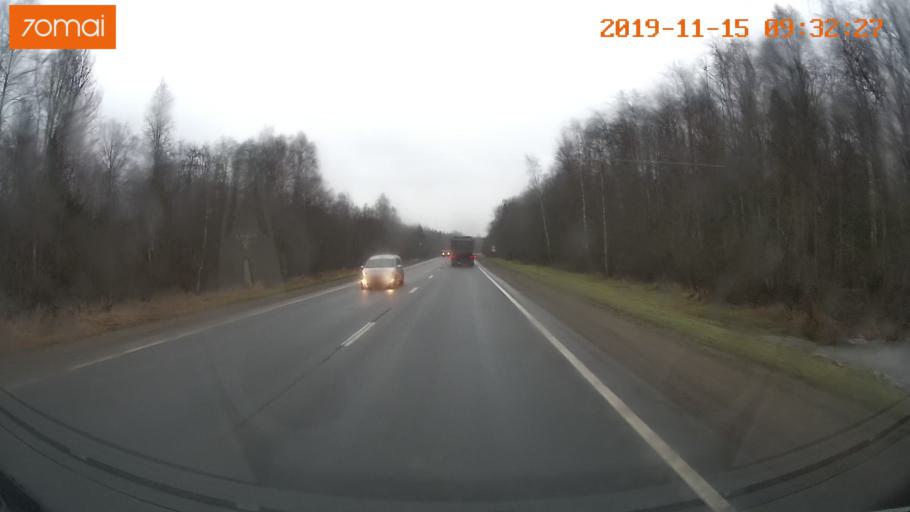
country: RU
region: Vologda
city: Sheksna
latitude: 59.2715
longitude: 38.3356
